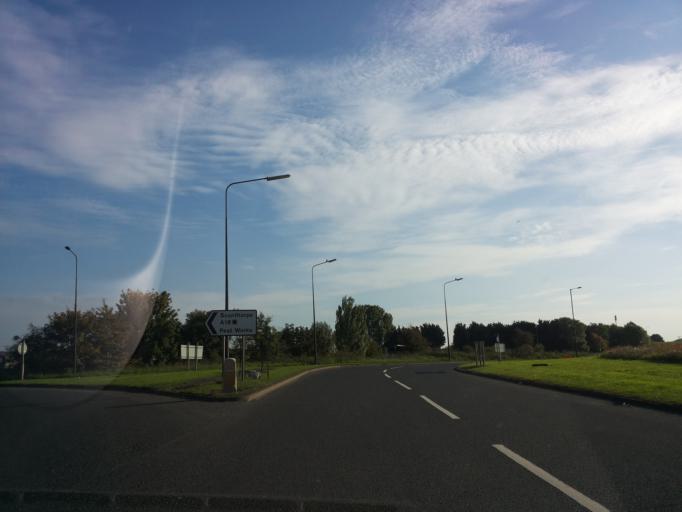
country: GB
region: England
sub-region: Doncaster
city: Hatfield
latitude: 53.5924
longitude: -0.9612
